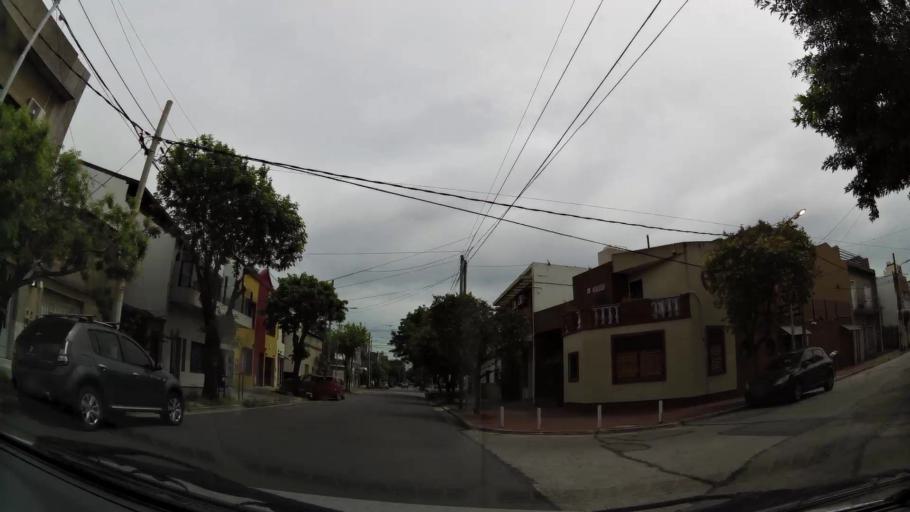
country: AR
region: Buenos Aires
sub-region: Partido de Avellaneda
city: Avellaneda
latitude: -34.6719
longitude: -58.3576
